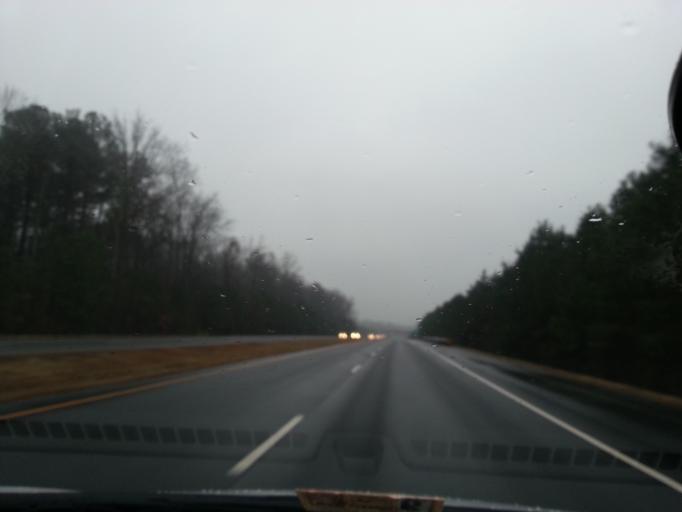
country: US
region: North Carolina
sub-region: Currituck County
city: Moyock
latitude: 36.6383
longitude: -76.2182
